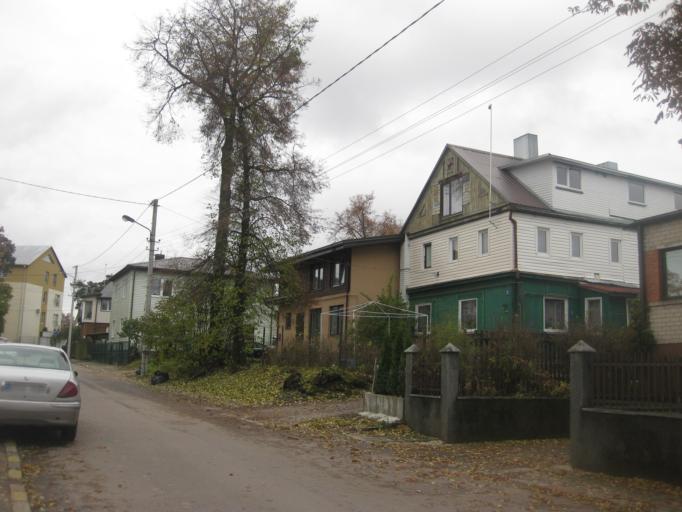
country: LT
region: Kauno apskritis
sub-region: Kaunas
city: Kaunas
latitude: 54.9095
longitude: 23.9133
